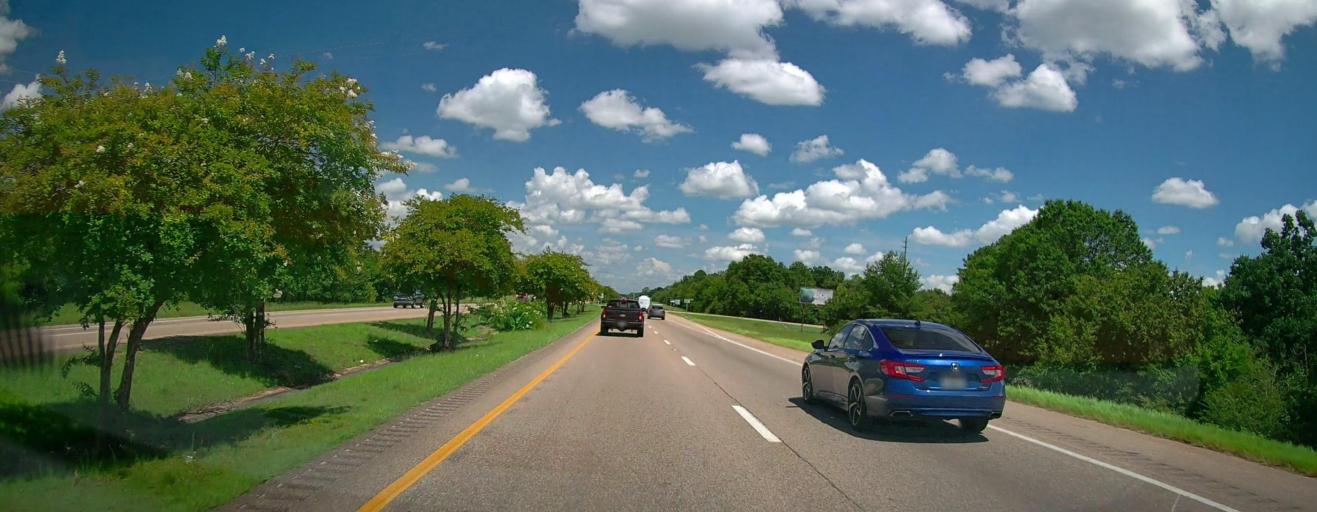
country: US
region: Alabama
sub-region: Montgomery County
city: Montgomery
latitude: 32.4229
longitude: -86.2762
